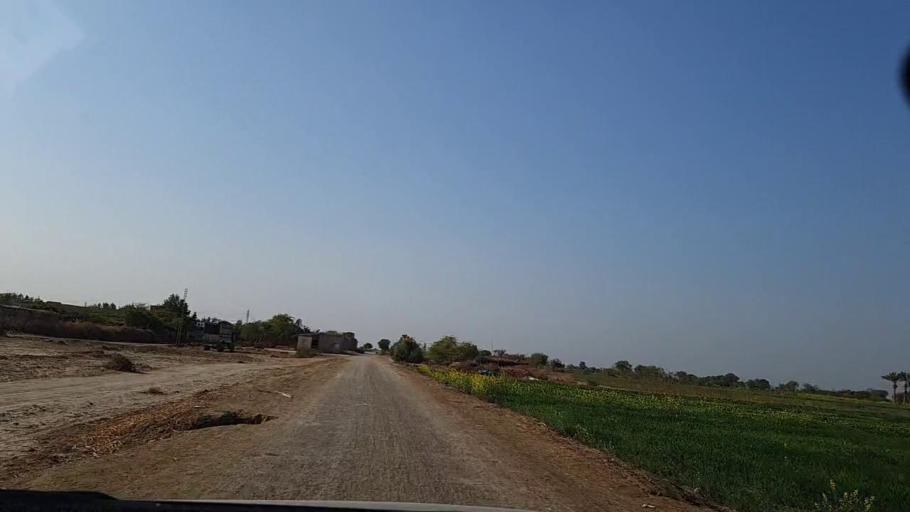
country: PK
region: Sindh
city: Mirwah Gorchani
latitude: 25.2219
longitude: 68.9913
